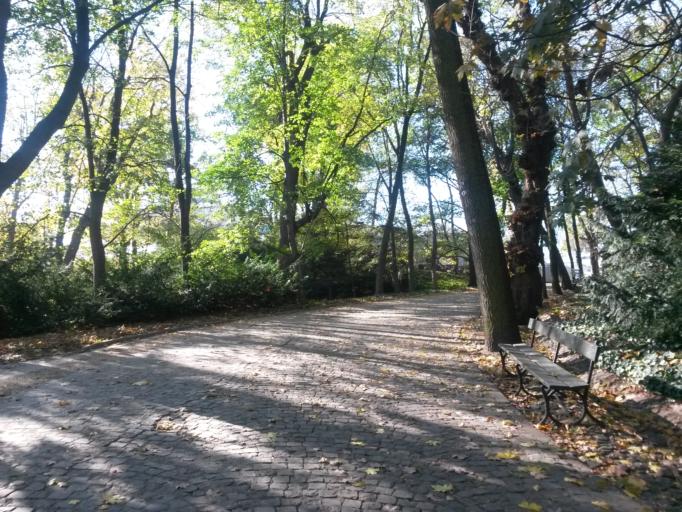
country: PL
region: Masovian Voivodeship
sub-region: Warszawa
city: Srodmiescie
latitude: 52.2139
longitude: 21.0287
